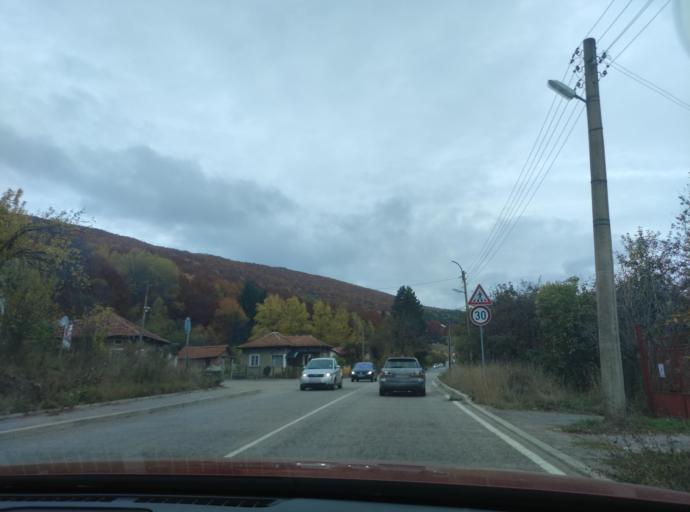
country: BG
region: Sofiya
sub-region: Obshtina Godech
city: Godech
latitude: 43.0876
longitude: 23.1001
